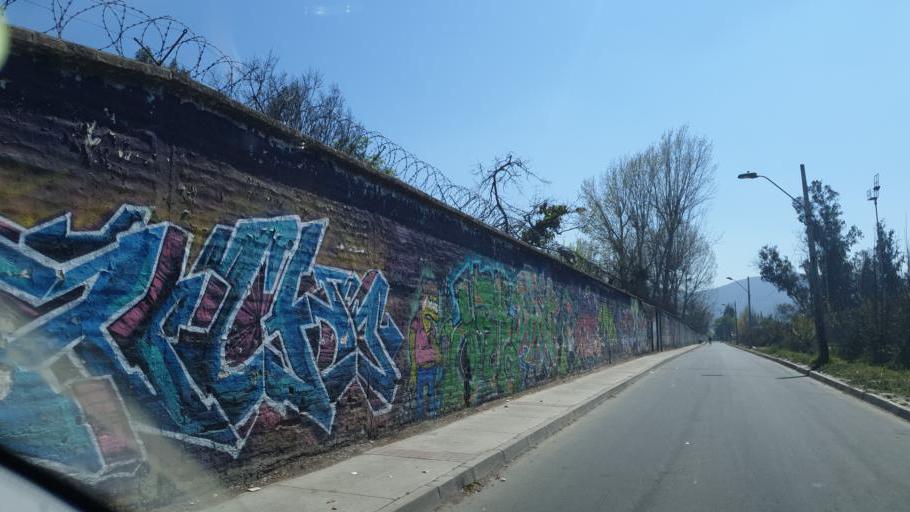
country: CL
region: Santiago Metropolitan
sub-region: Provincia de Talagante
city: Talagante
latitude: -33.6579
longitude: -70.9258
